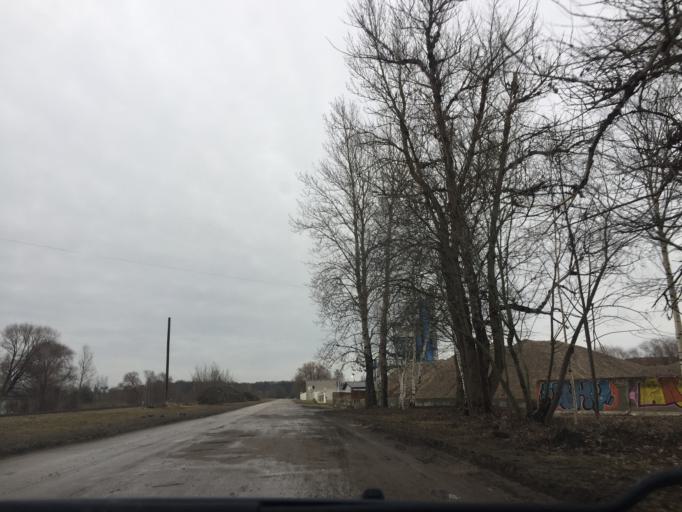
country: LV
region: Riga
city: Riga
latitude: 56.9785
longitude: 24.1254
